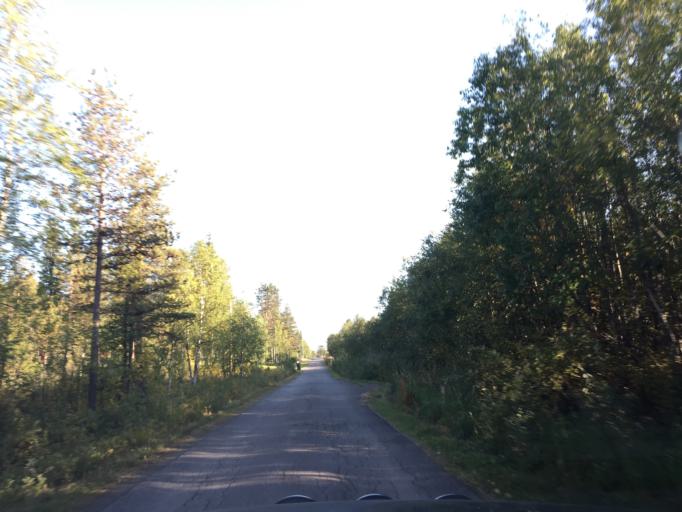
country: SE
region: Norrbotten
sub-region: Gallivare Kommun
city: Malmberget
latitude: 67.6532
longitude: 21.0395
